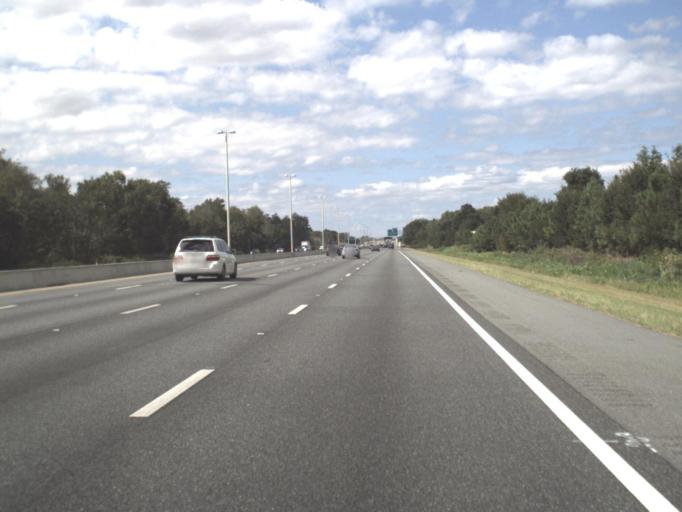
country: US
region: Florida
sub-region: Orange County
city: Winter Garden
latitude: 28.5454
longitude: -81.5913
